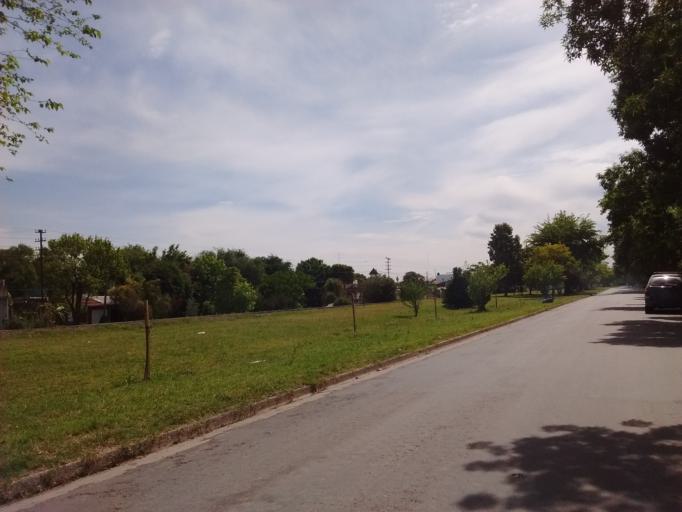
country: AR
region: Santa Fe
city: Funes
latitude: -32.9178
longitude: -60.8053
